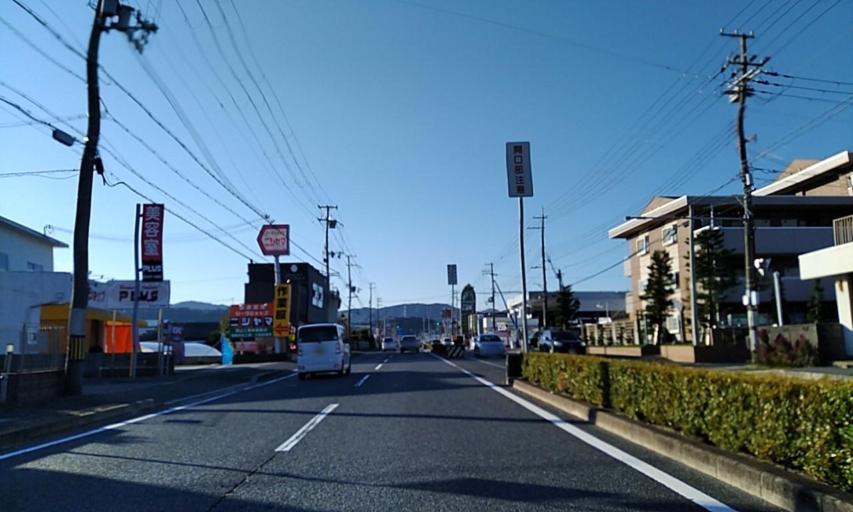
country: JP
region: Wakayama
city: Kainan
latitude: 34.1764
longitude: 135.1865
